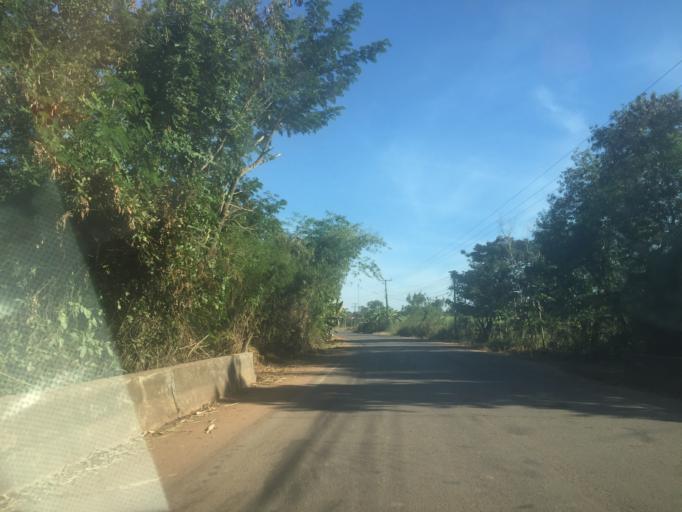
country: TH
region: Kalasin
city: Tha Khantho
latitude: 16.9744
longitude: 103.2619
